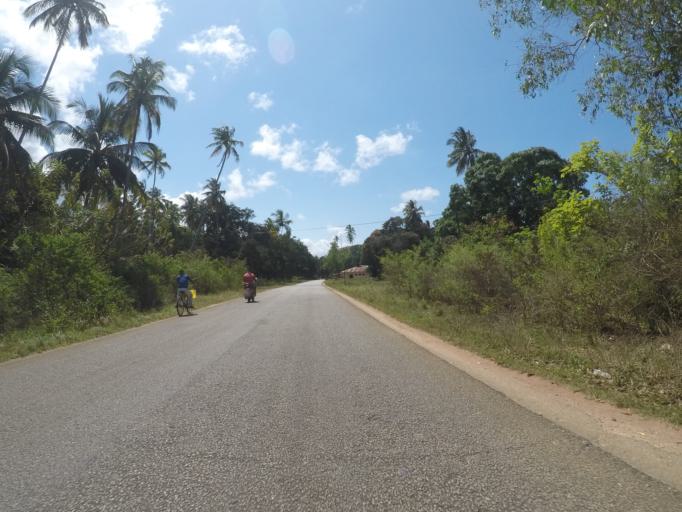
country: TZ
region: Zanzibar Central/South
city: Koani
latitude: -6.1485
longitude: 39.3363
